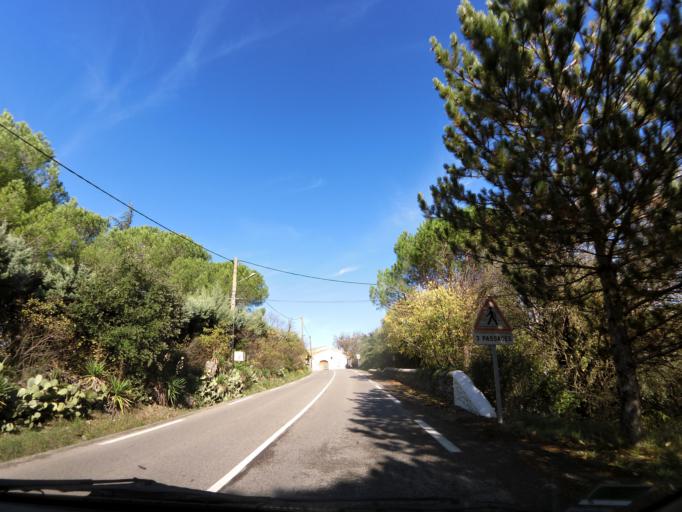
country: FR
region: Languedoc-Roussillon
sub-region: Departement du Gard
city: Saint-Mamert-du-Gard
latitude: 43.8795
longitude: 4.0963
